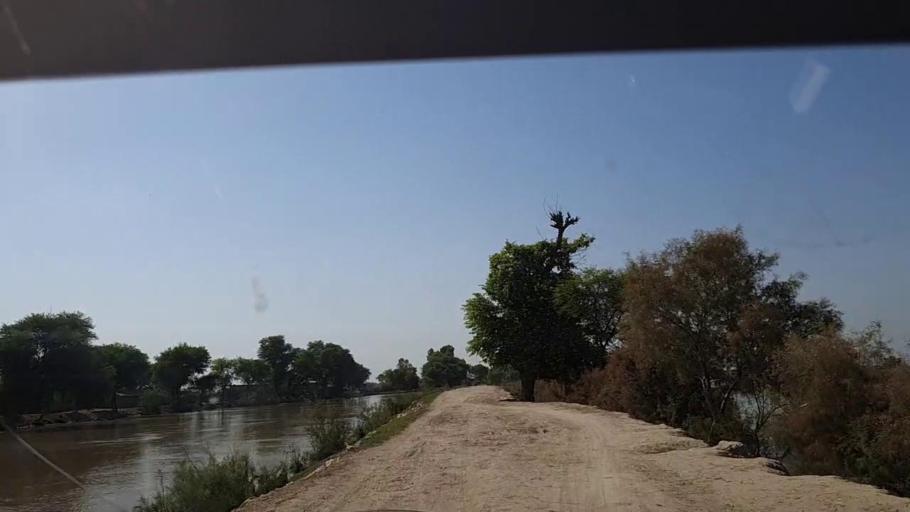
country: PK
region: Sindh
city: Ghauspur
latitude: 28.1803
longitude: 69.0876
